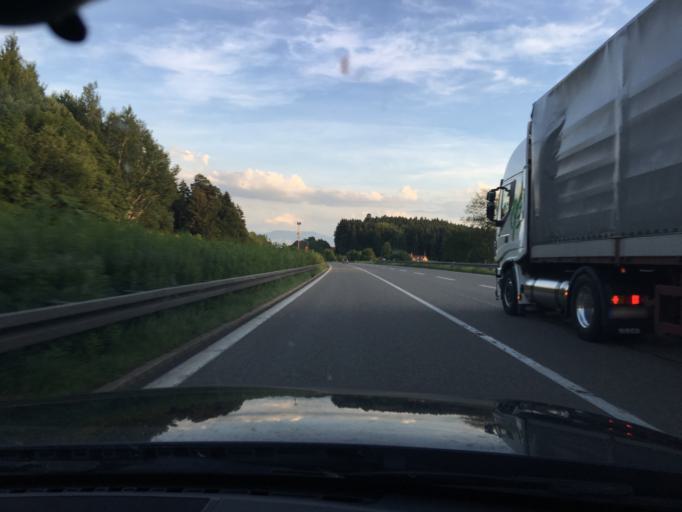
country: DE
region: Bavaria
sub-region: Swabia
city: Weissensberg
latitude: 47.5792
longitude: 9.7350
